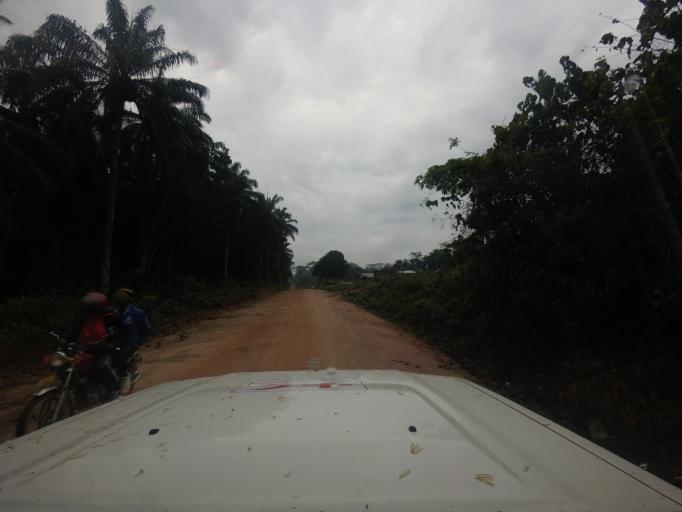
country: LR
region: Lofa
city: Voinjama
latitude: 8.3877
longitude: -9.8222
